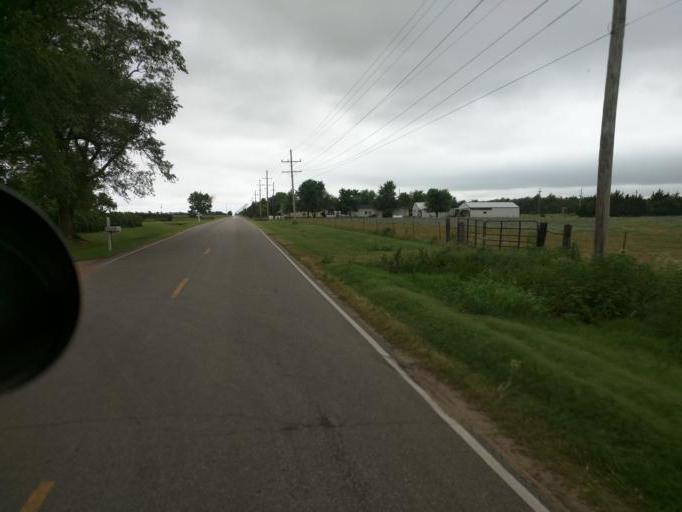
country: US
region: Kansas
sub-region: Reno County
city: Haven
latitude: 37.9320
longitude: -97.8852
